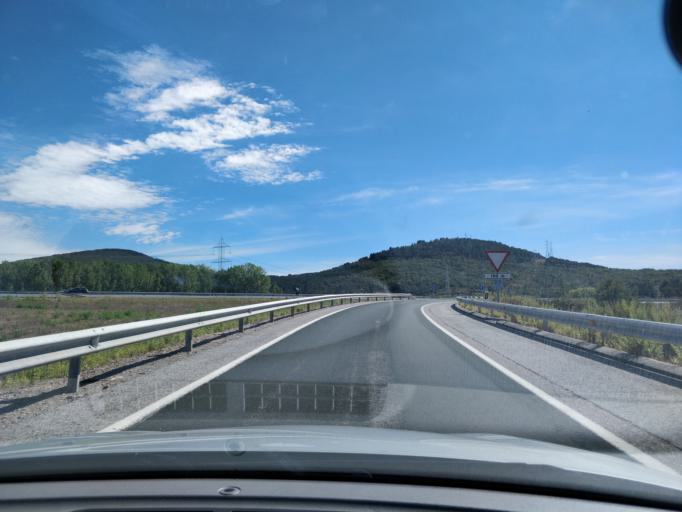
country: ES
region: Castille and Leon
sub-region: Provincia de Leon
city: Ponferrada
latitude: 42.5790
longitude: -6.6055
